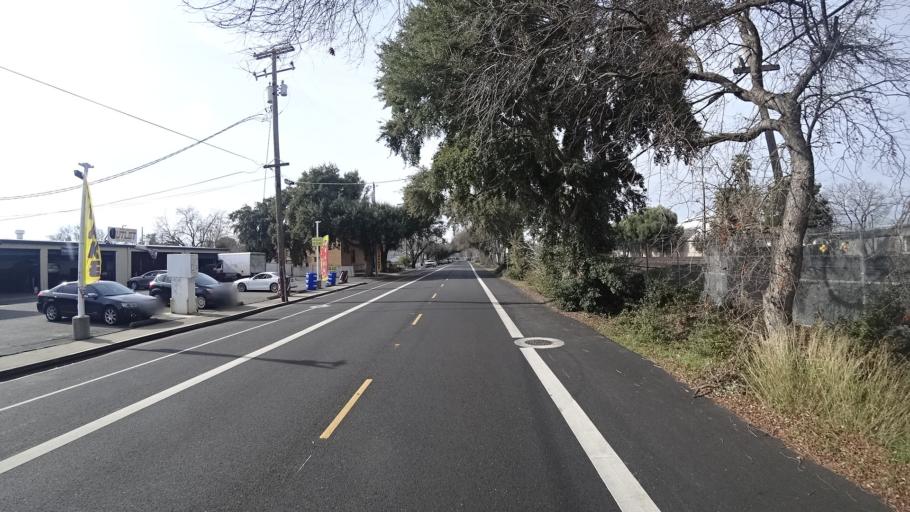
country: US
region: California
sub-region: Yolo County
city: Davis
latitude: 38.5451
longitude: -121.7306
